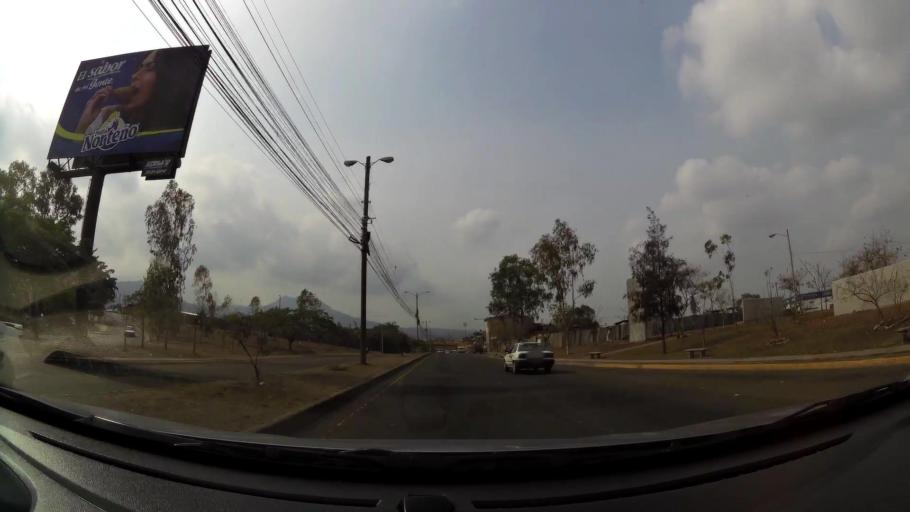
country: HN
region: Francisco Morazan
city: Santa Lucia
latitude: 14.1019
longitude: -87.1592
